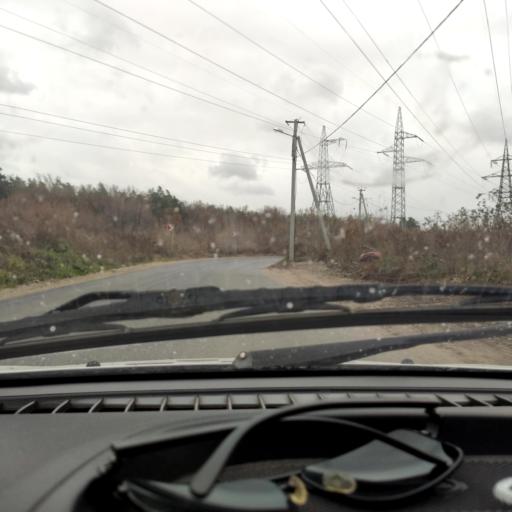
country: RU
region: Samara
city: Zhigulevsk
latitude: 53.5211
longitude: 49.4864
